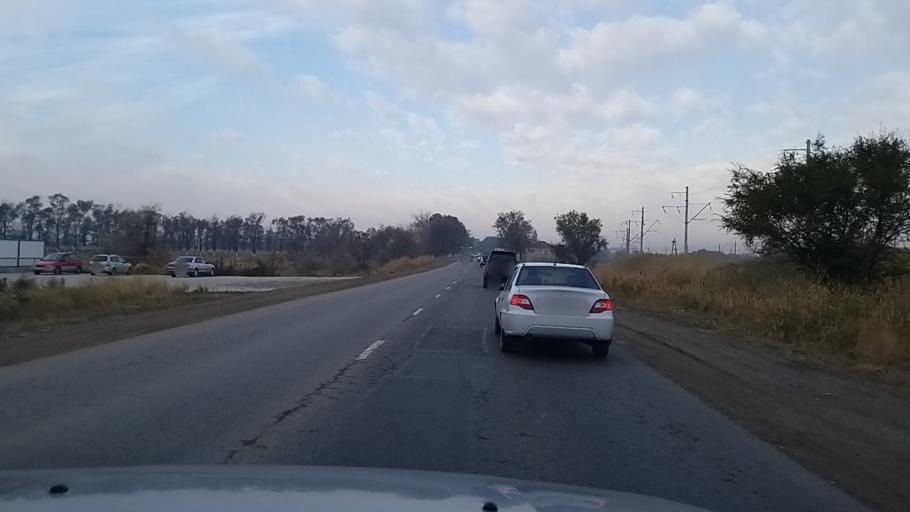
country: KZ
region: Almaty Oblysy
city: Burunday
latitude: 43.3586
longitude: 76.7717
